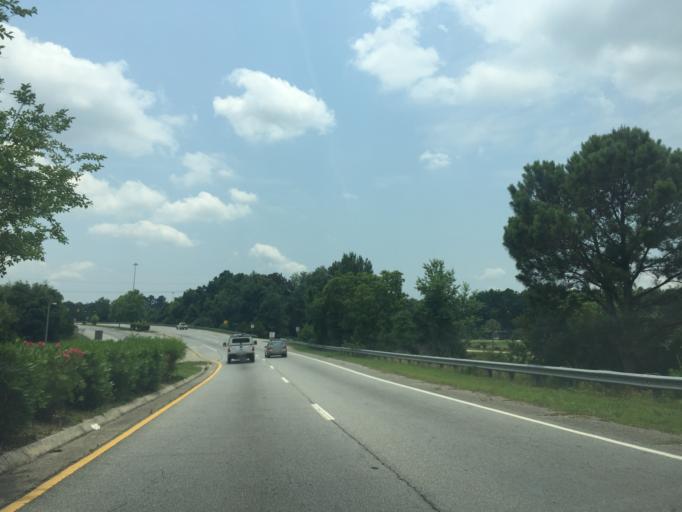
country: US
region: Georgia
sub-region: Chatham County
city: Garden City
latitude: 32.0419
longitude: -81.1657
